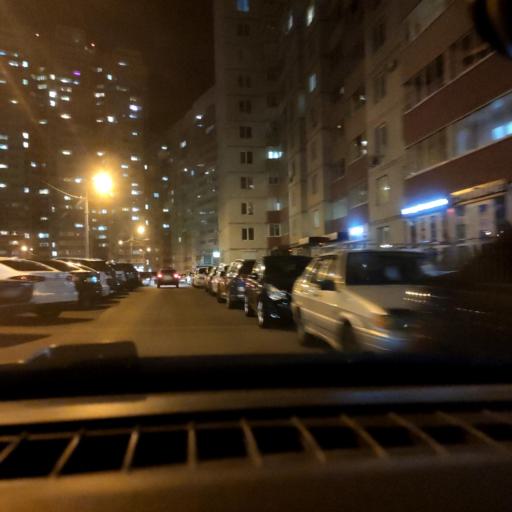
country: RU
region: Voronezj
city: Voronezh
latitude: 51.7114
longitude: 39.2000
